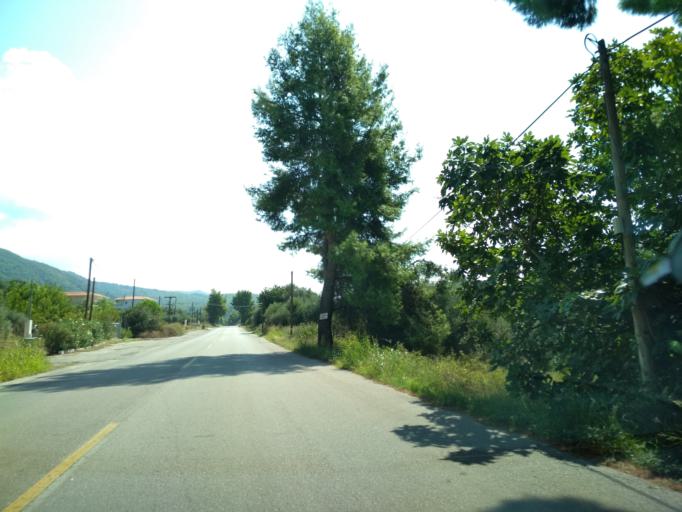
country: GR
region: Central Greece
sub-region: Nomos Evvoias
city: Roviai
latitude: 38.8307
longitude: 23.2072
